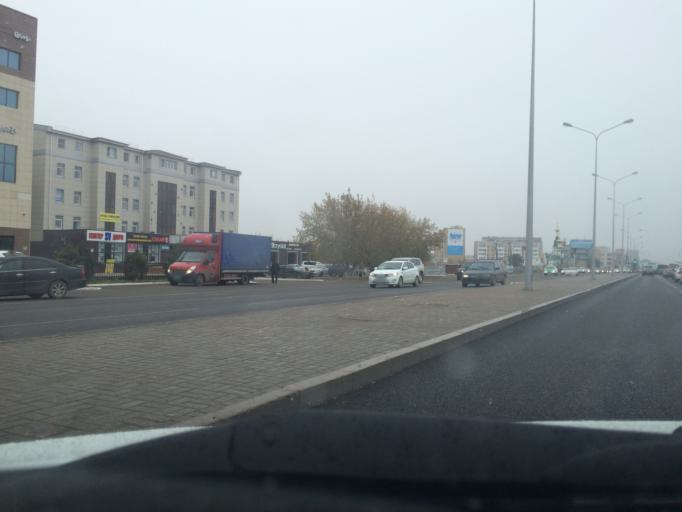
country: KZ
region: Astana Qalasy
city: Astana
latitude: 51.1756
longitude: 71.3989
